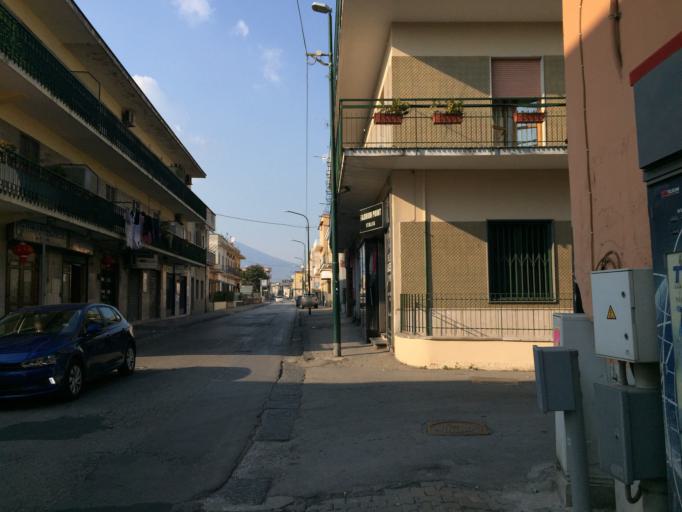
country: IT
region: Campania
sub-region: Provincia di Napoli
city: Pompei
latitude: 40.7521
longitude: 14.4999
